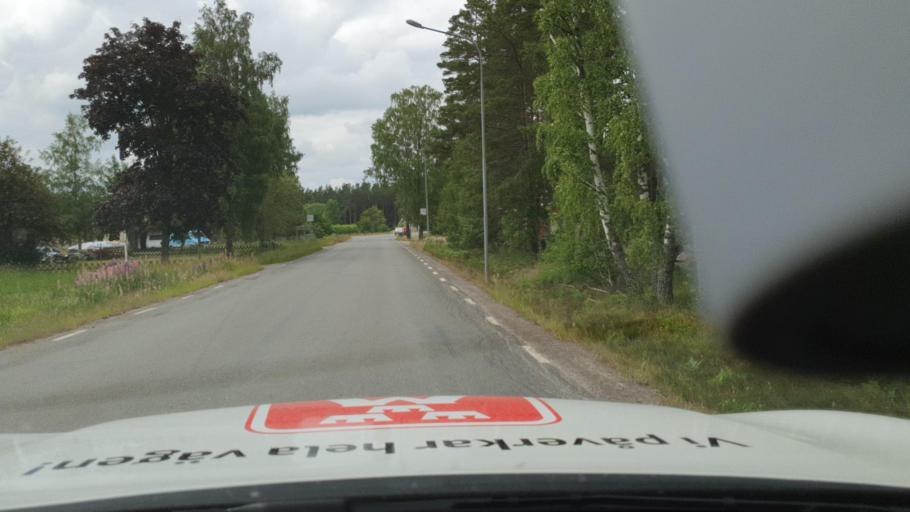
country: SE
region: Vaestra Goetaland
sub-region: Tidaholms Kommun
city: Tidaholm
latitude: 58.1274
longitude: 14.0486
